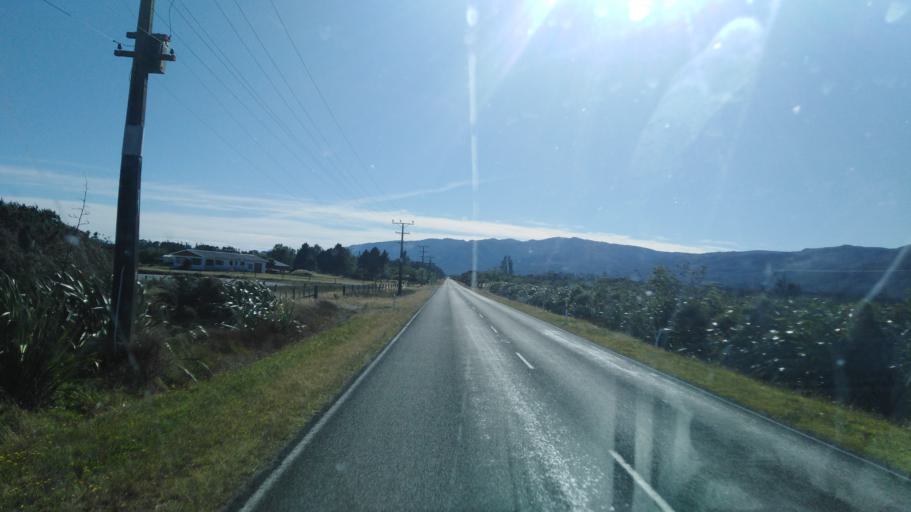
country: NZ
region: West Coast
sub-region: Buller District
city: Westport
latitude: -41.7478
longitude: 171.6793
